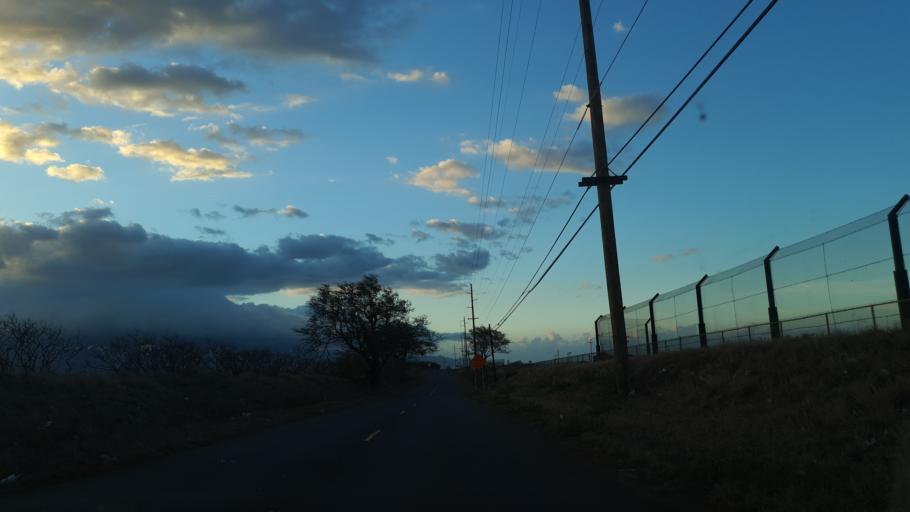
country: US
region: Hawaii
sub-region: Maui County
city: Kahului
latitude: 20.8564
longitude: -156.4228
